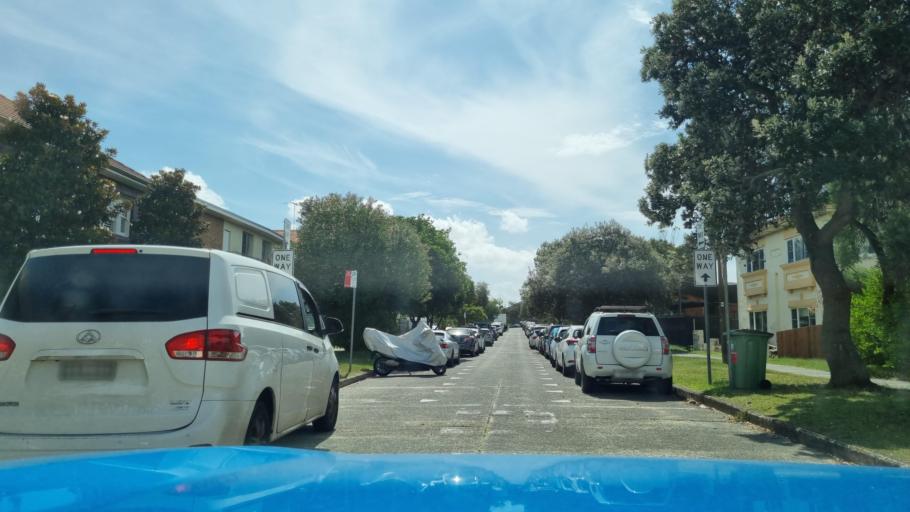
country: AU
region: New South Wales
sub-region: Waverley
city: North Bondi
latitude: -33.8873
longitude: 151.2790
